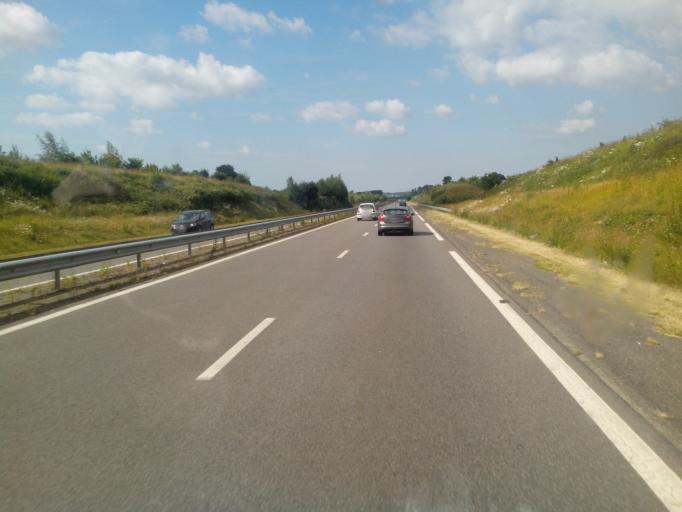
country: FR
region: Brittany
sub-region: Departement d'Ille-et-Vilaine
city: Betton
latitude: 48.1707
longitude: -1.6261
